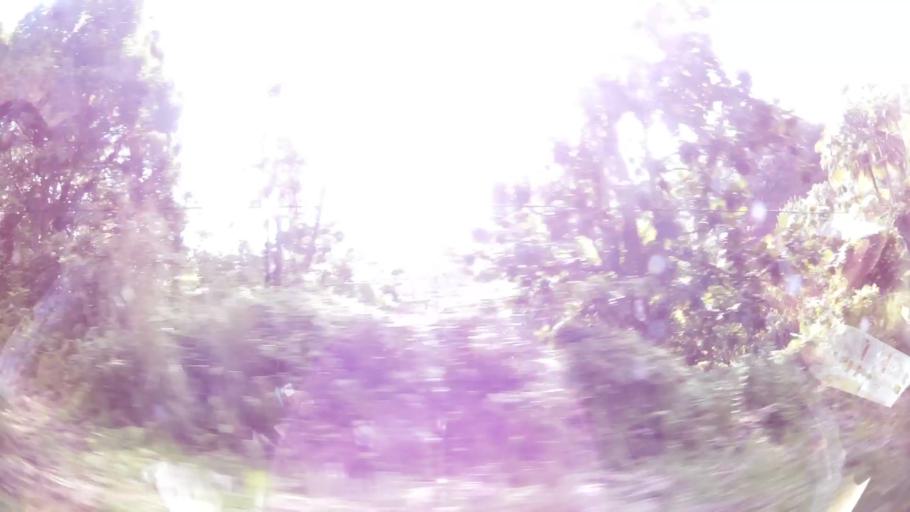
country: DM
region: Saint David
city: Castle Bruce
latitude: 15.4740
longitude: -61.2515
